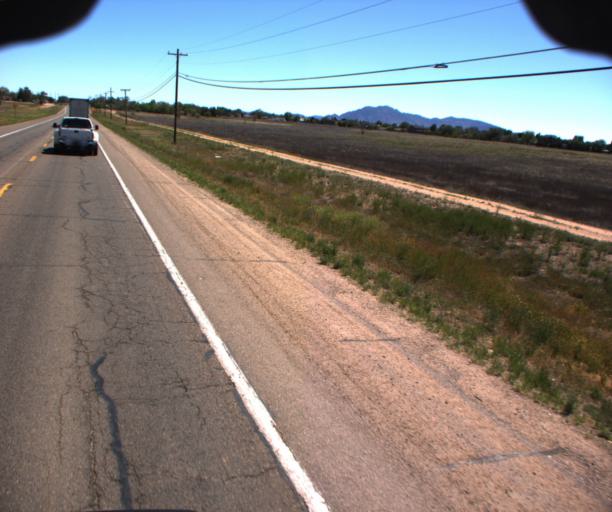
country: US
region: Arizona
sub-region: Yavapai County
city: Chino Valley
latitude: 34.7817
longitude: -112.4525
